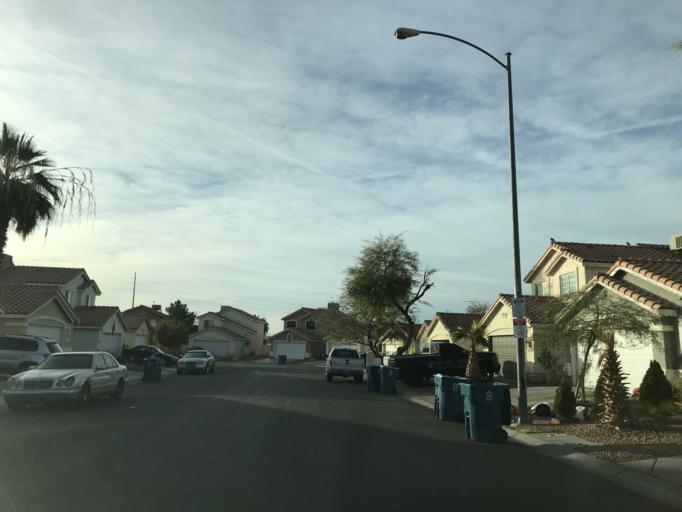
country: US
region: Nevada
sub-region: Clark County
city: Nellis Air Force Base
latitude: 36.2443
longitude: -115.0581
